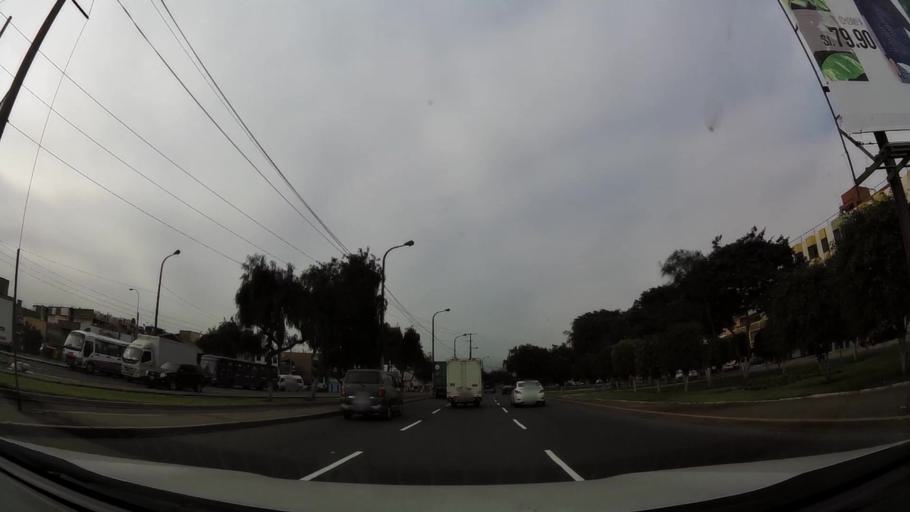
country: PE
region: Callao
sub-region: Callao
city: Callao
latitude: -12.0134
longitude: -77.0947
